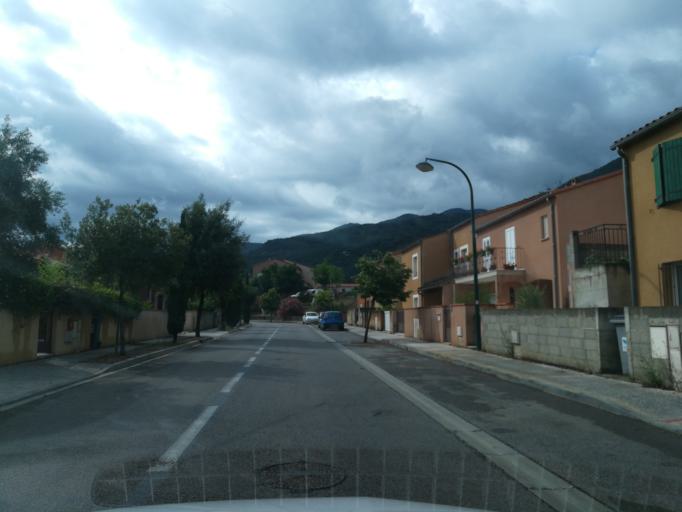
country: FR
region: Languedoc-Roussillon
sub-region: Departement des Pyrenees-Orientales
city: Ceret
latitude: 42.4857
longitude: 2.7421
